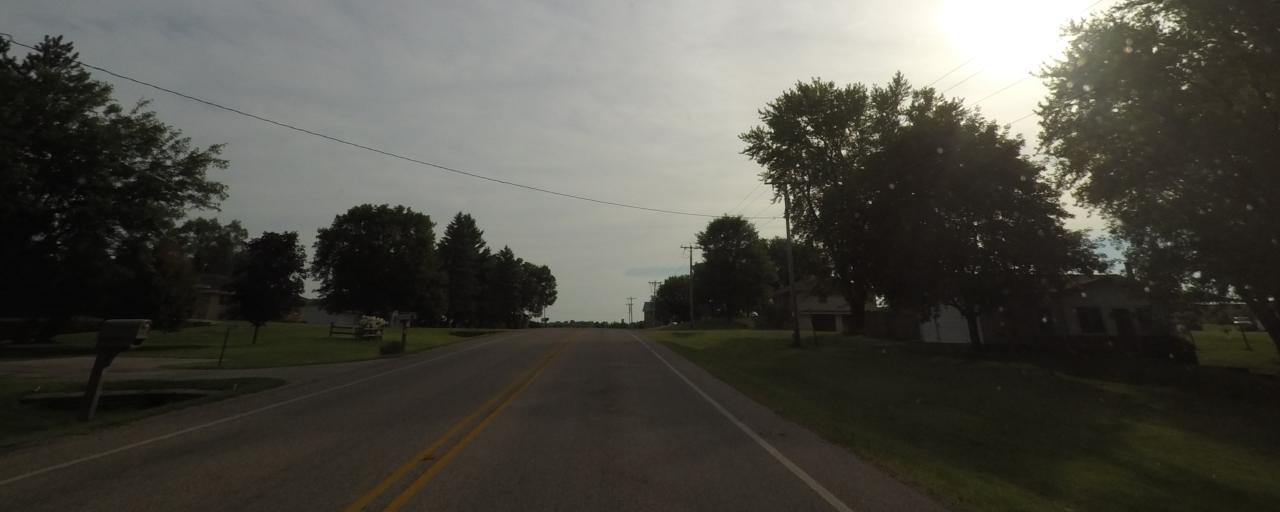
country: US
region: Wisconsin
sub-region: Dane County
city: Waunakee
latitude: 43.1944
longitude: -89.5625
